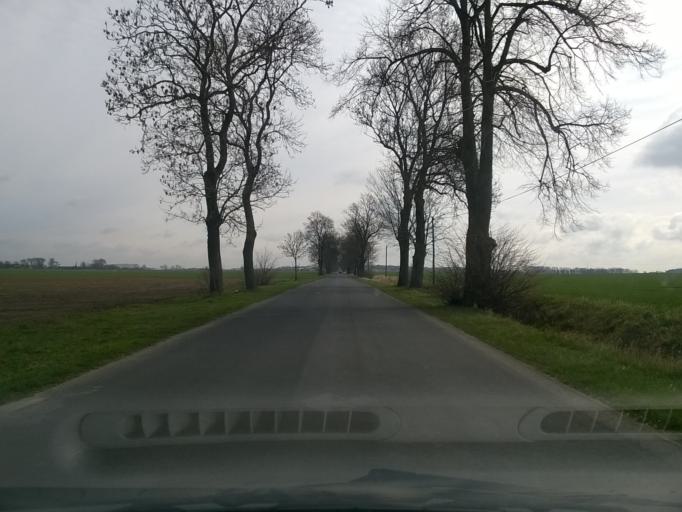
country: PL
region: Kujawsko-Pomorskie
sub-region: Powiat nakielski
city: Kcynia
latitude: 52.9900
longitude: 17.4374
